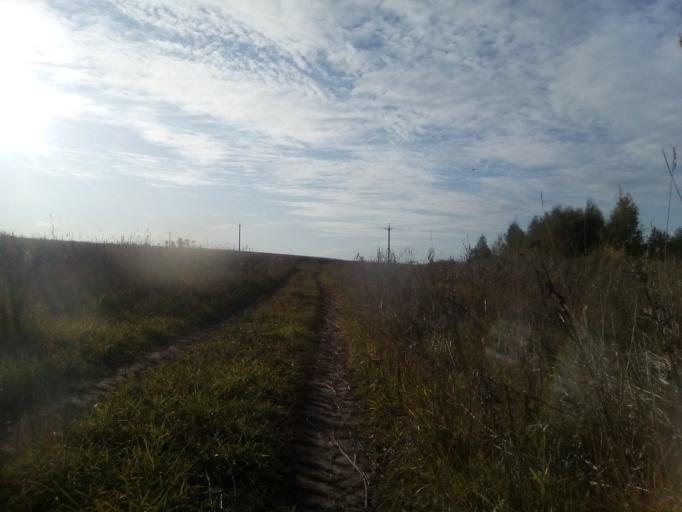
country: RU
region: Moskovskaya
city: Filimonki
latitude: 55.5452
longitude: 37.3752
